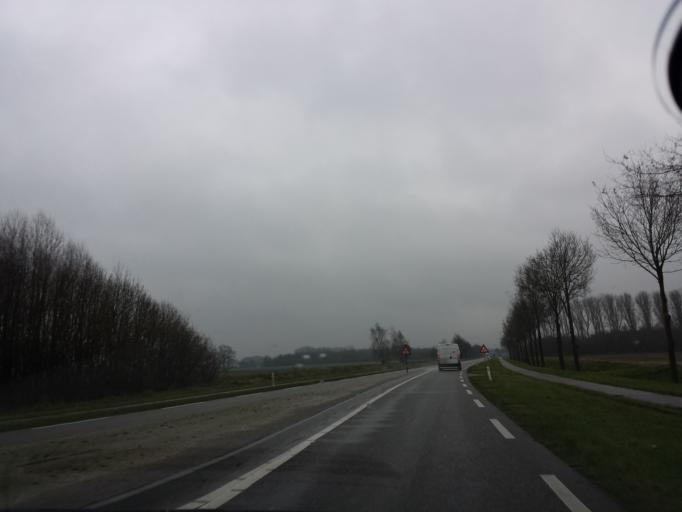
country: NL
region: Limburg
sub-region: Gemeente Peel en Maas
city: Maasbree
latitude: 51.3671
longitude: 5.9997
